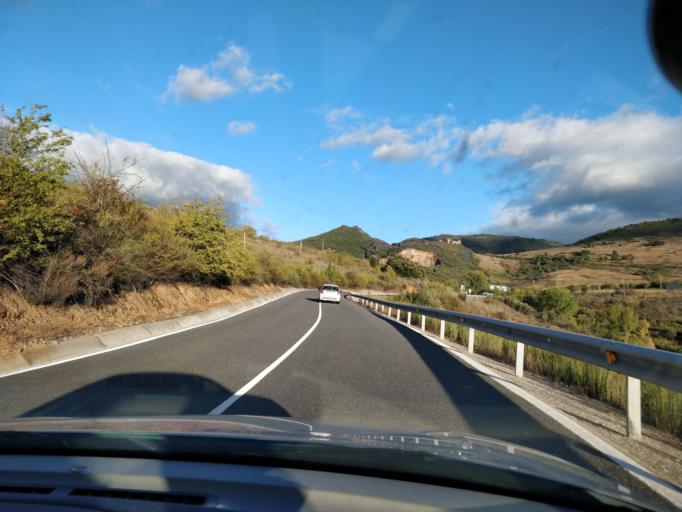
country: ES
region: Castille and Leon
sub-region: Provincia de Leon
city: Borrenes
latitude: 42.4927
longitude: -6.7081
